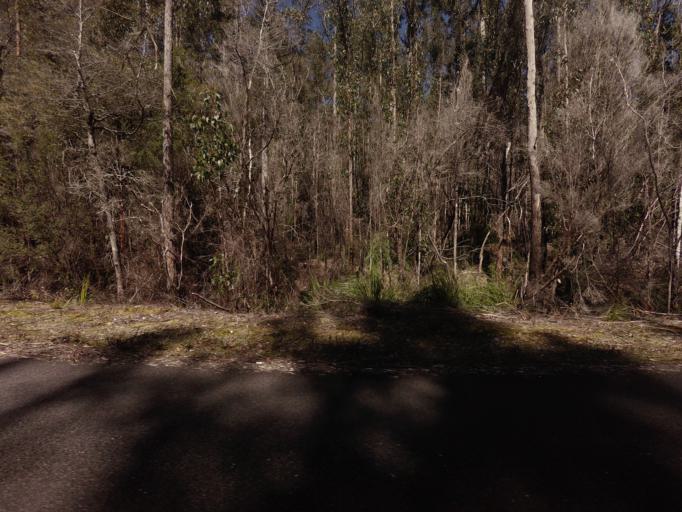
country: AU
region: Tasmania
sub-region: Huon Valley
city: Geeveston
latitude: -42.8422
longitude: 146.2528
